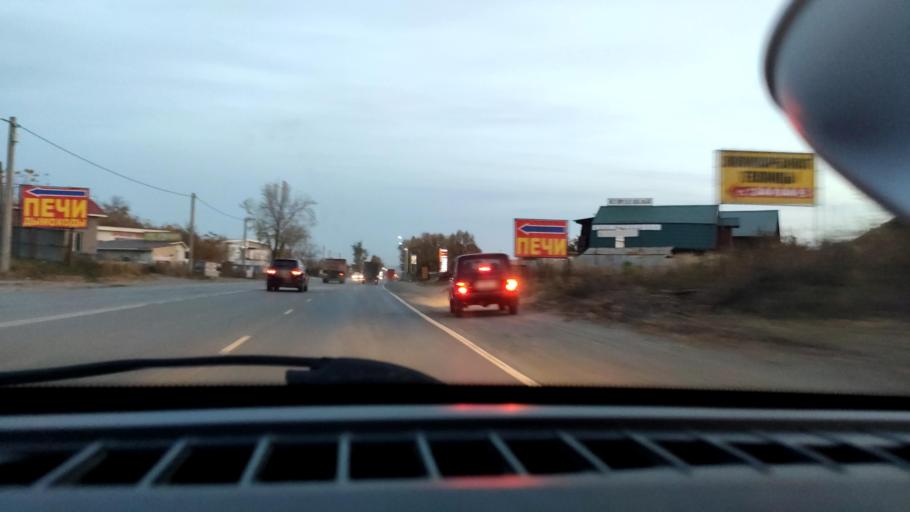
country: RU
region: Samara
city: Petra-Dubrava
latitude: 53.2689
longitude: 50.2793
